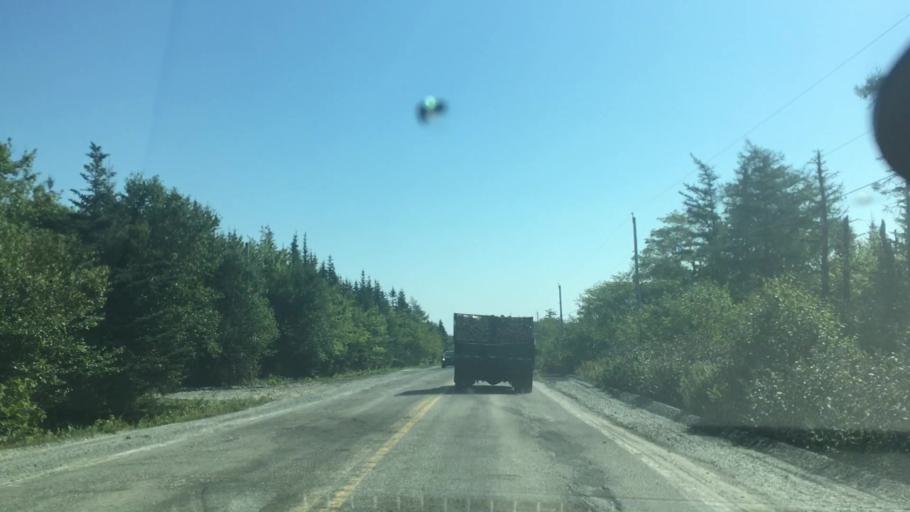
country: CA
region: Nova Scotia
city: New Glasgow
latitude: 44.8989
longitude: -62.4349
